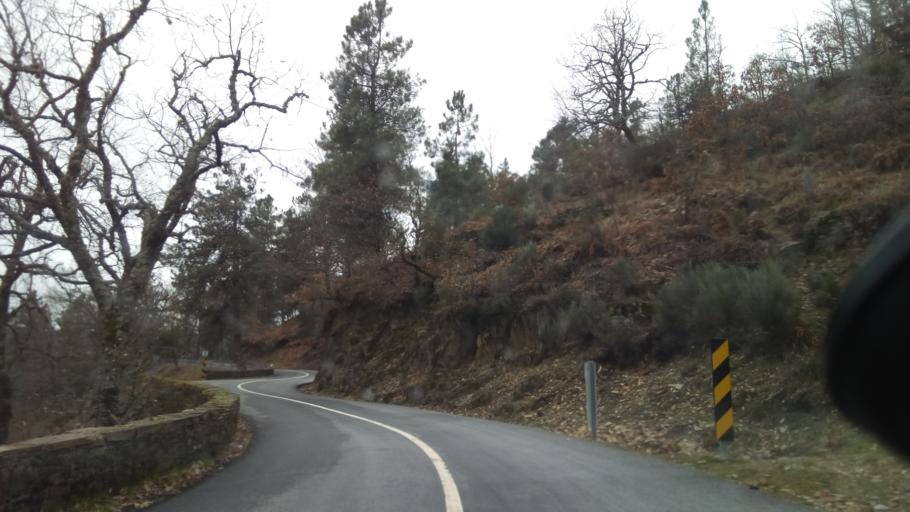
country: PT
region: Guarda
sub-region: Manteigas
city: Manteigas
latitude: 40.4156
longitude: -7.5291
